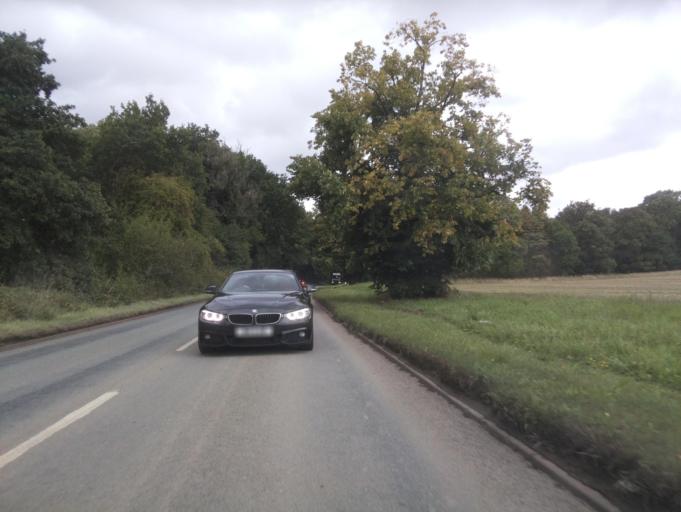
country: GB
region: England
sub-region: Staffordshire
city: Eccleshall
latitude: 52.8986
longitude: -2.2149
